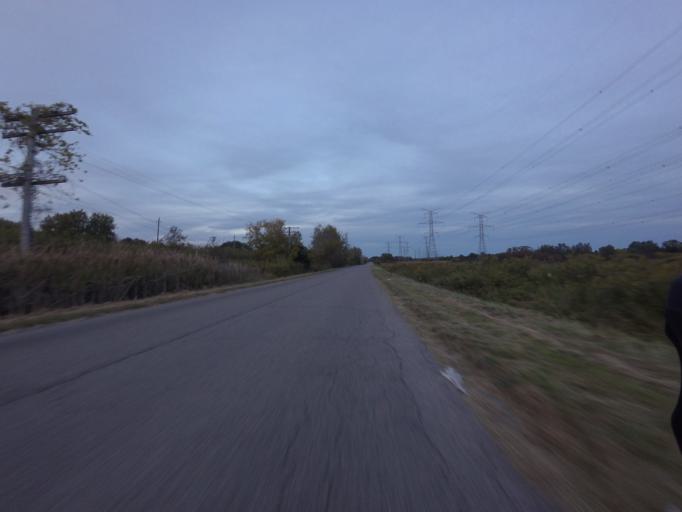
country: CA
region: Ontario
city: Oshawa
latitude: 43.9031
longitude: -78.6184
